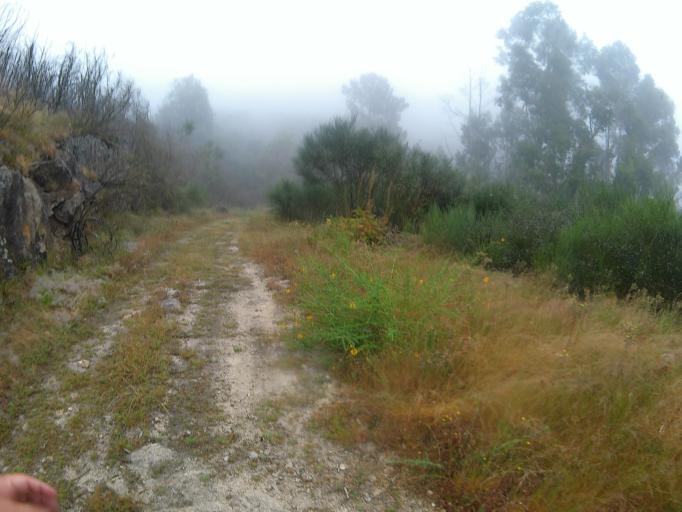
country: PT
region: Viana do Castelo
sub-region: Ponte de Lima
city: Ponte de Lima
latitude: 41.7064
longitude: -8.6041
